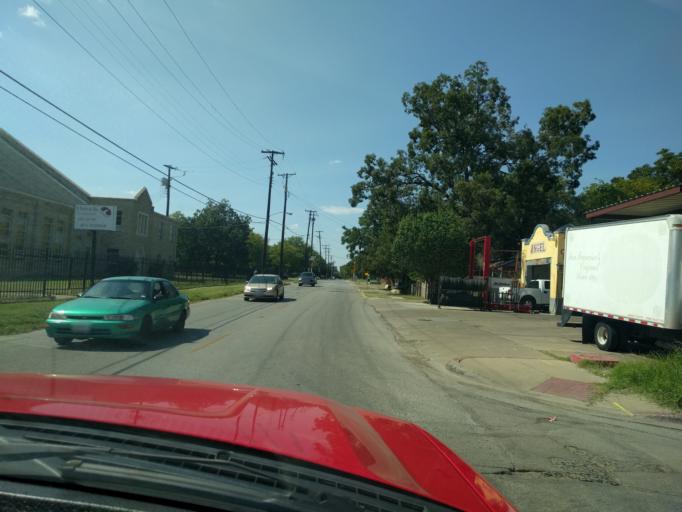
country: US
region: Texas
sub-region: Dallas County
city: Dallas
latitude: 32.7926
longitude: -96.7606
